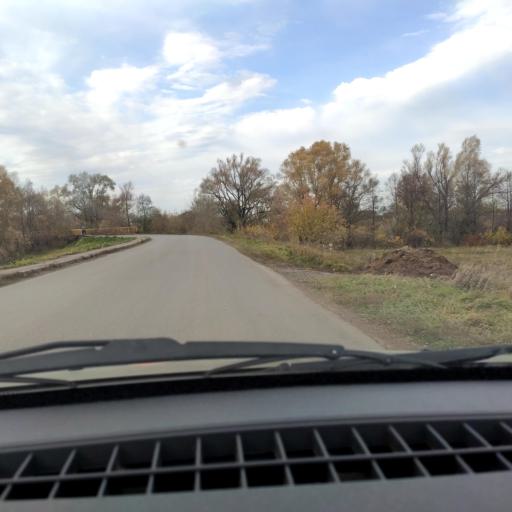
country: RU
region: Bashkortostan
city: Ufa
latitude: 54.6100
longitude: 55.9040
